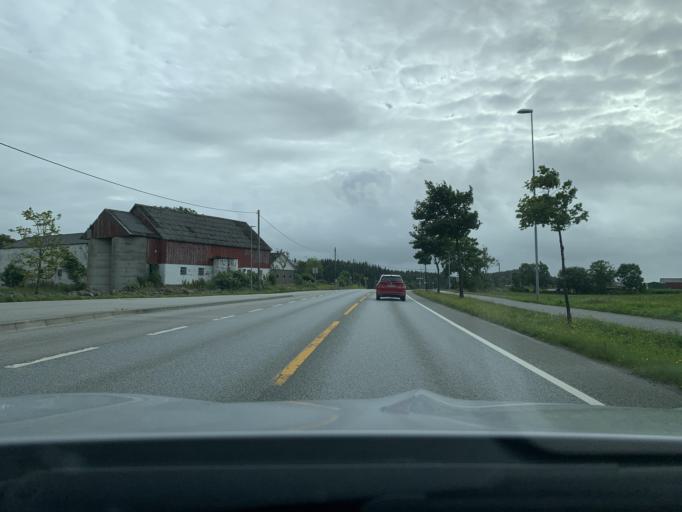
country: NO
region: Rogaland
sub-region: Sandnes
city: Sandnes
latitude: 58.8073
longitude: 5.6907
